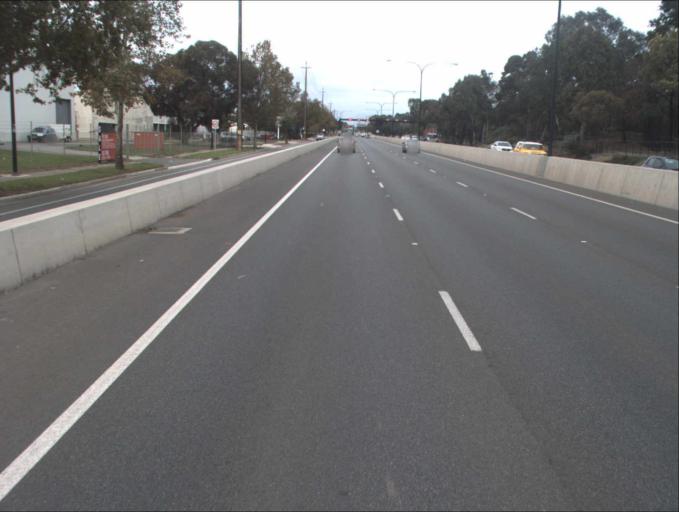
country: AU
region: South Australia
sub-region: Charles Sturt
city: Woodville
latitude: -34.8667
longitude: 138.5707
